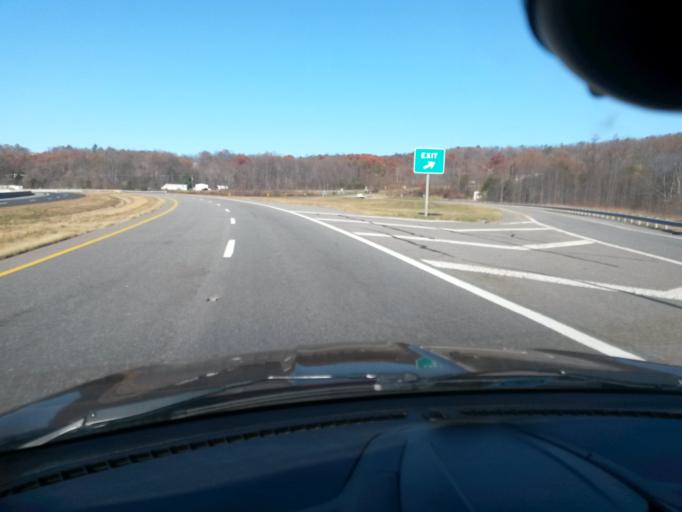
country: US
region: Virginia
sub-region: Patrick County
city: Stuart
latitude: 36.6493
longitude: -80.2681
